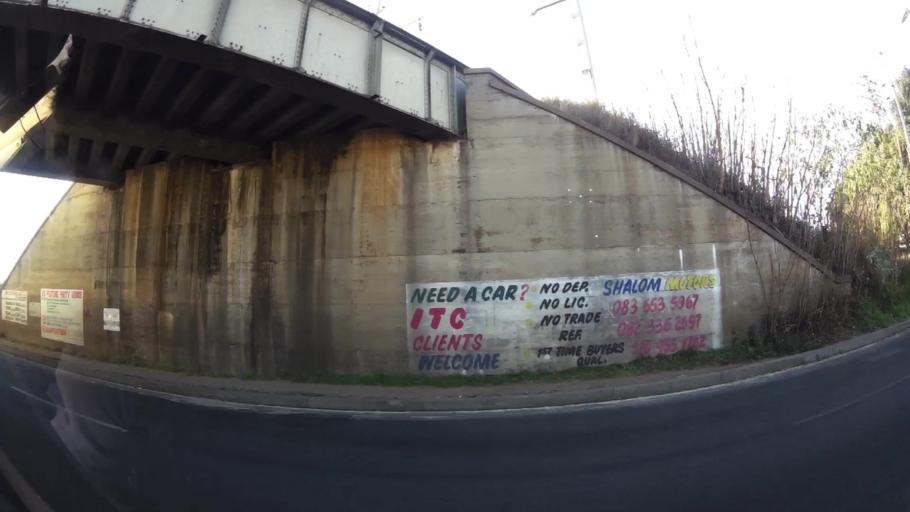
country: ZA
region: Gauteng
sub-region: West Rand District Municipality
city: Krugersdorp
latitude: -26.1179
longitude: 27.8015
